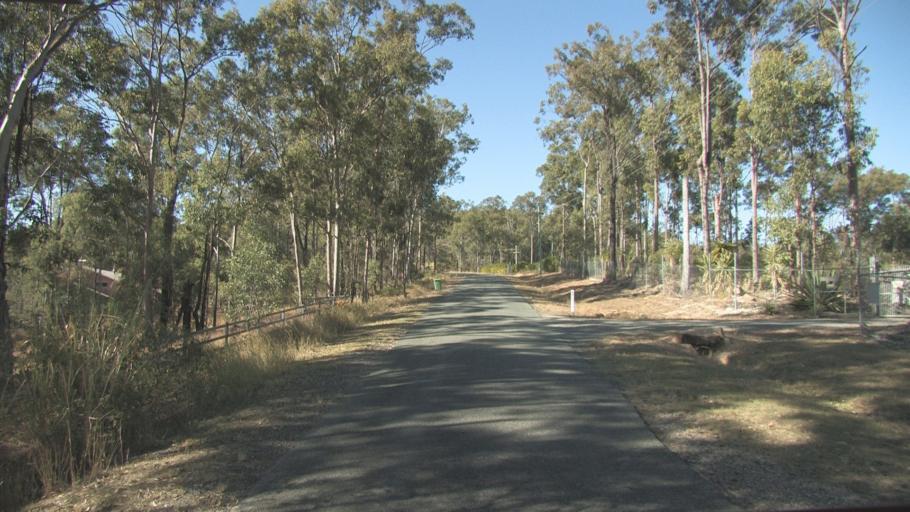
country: AU
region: Queensland
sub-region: Logan
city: Cedar Vale
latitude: -27.8449
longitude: 153.0709
